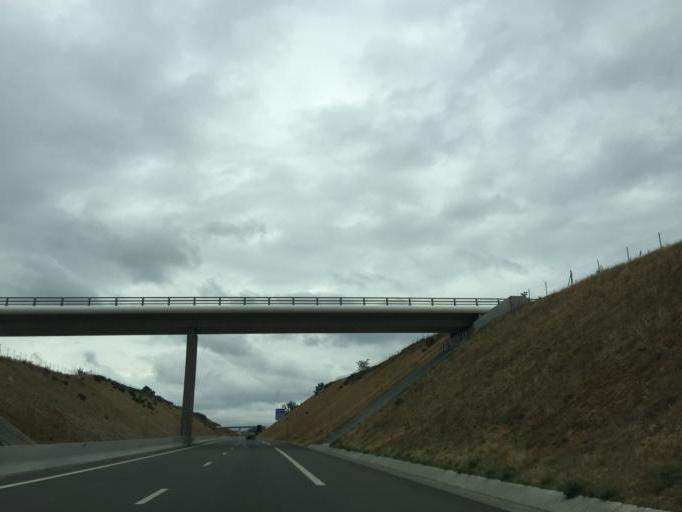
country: FR
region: Rhone-Alpes
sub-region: Departement de la Loire
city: Balbigny
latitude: 45.8427
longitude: 4.2076
